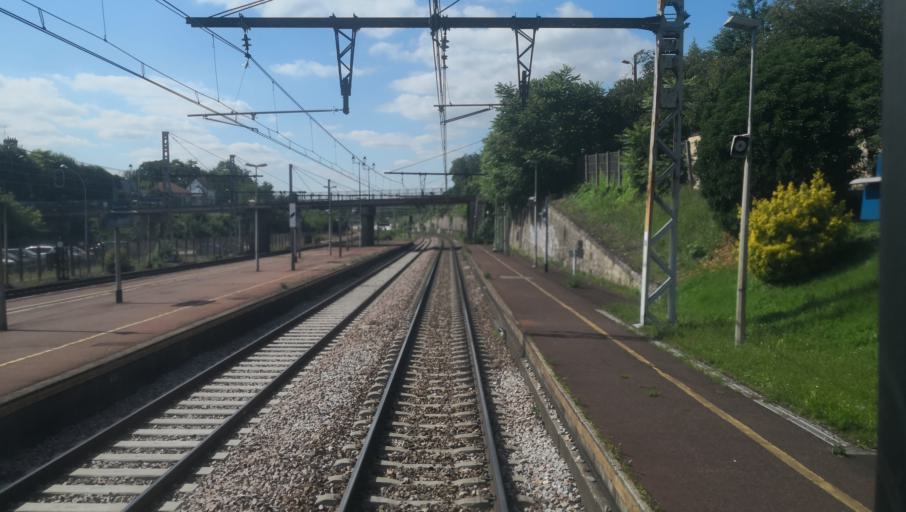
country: FR
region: Ile-de-France
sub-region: Departement de l'Essonne
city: Epinay-sous-Senart
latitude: 48.6998
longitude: 2.5064
